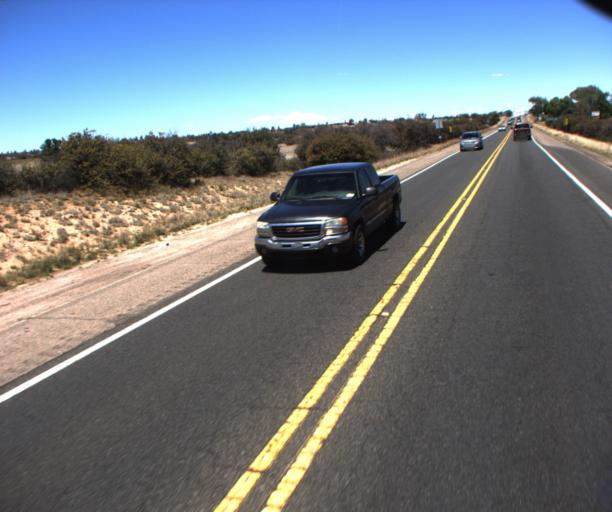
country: US
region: Arizona
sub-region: Yavapai County
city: Prescott
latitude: 34.6375
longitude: -112.4306
